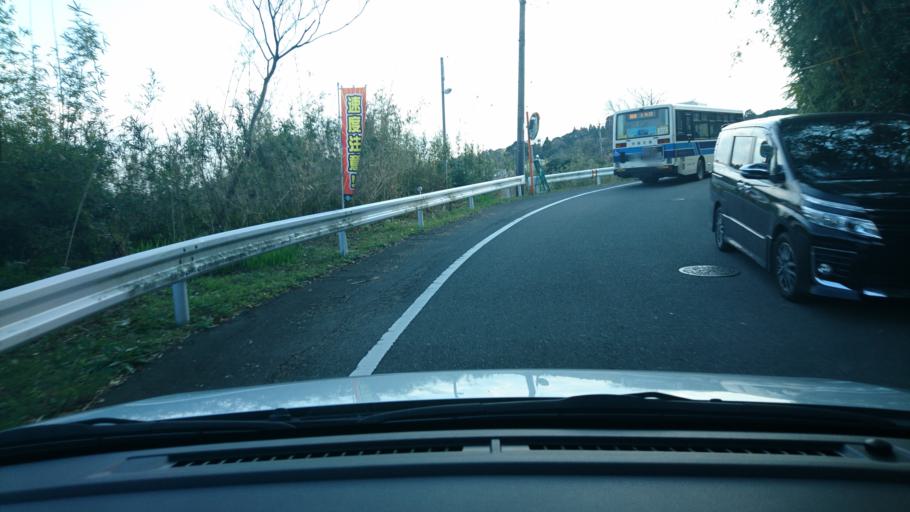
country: JP
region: Miyazaki
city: Miyazaki-shi
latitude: 31.8686
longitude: 131.4040
